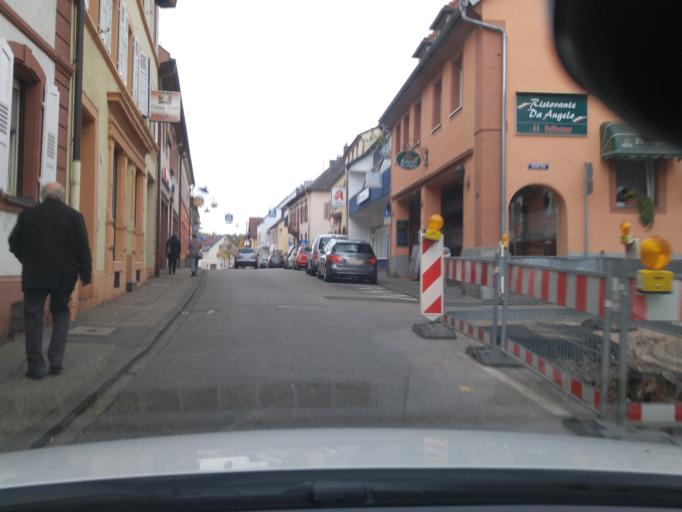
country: DE
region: Rheinland-Pfalz
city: Annweiler am Trifels
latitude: 49.2027
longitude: 7.9647
